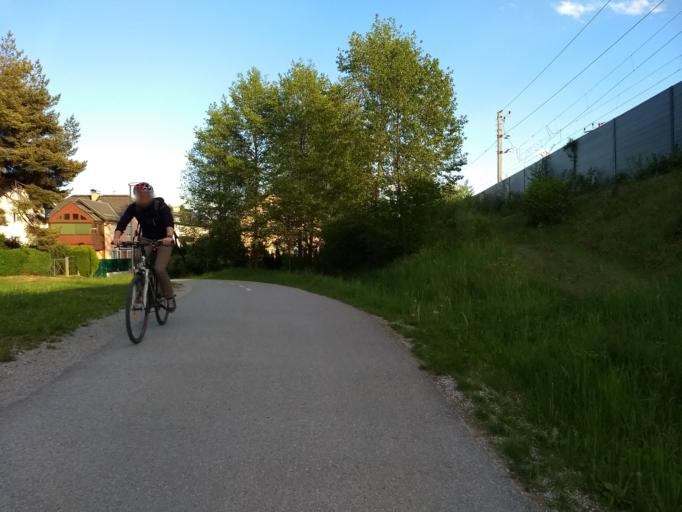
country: AT
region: Salzburg
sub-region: Politischer Bezirk Salzburg-Umgebung
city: Bergheim
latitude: 47.8112
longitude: 13.0175
